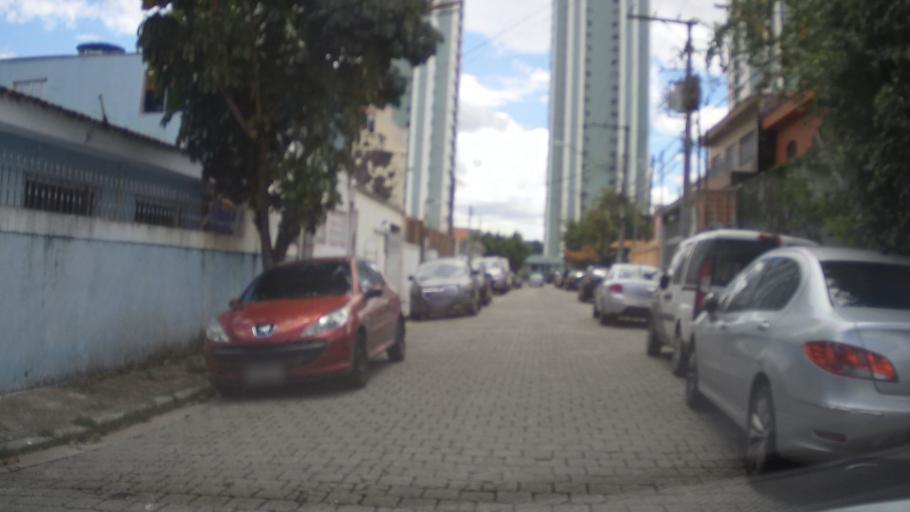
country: BR
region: Sao Paulo
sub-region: Guarulhos
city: Guarulhos
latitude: -23.4621
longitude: -46.5467
